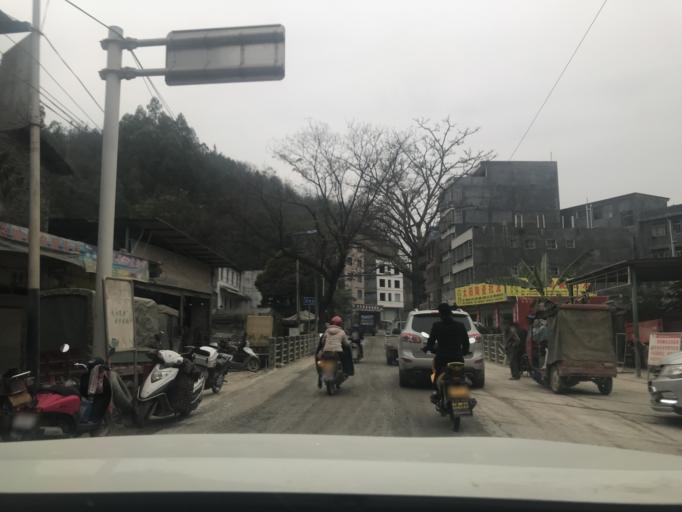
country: CN
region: Guangxi Zhuangzu Zizhiqu
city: Xinzhou
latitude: 24.9813
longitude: 105.8189
